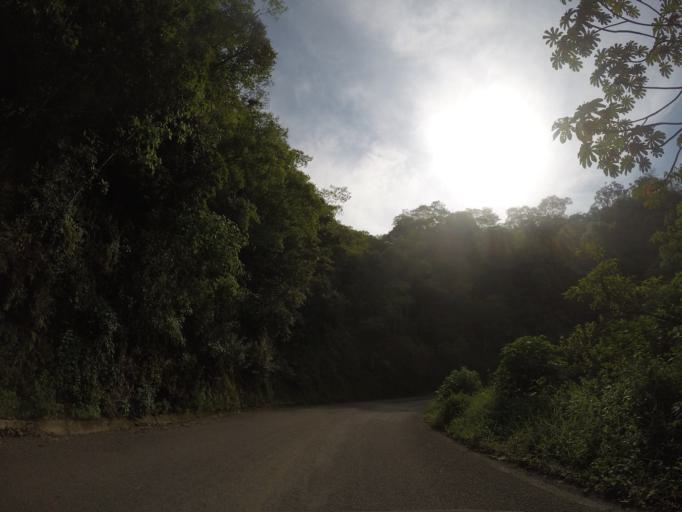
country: MX
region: Oaxaca
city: Pluma Hidalgo
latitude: 15.9337
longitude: -96.4293
